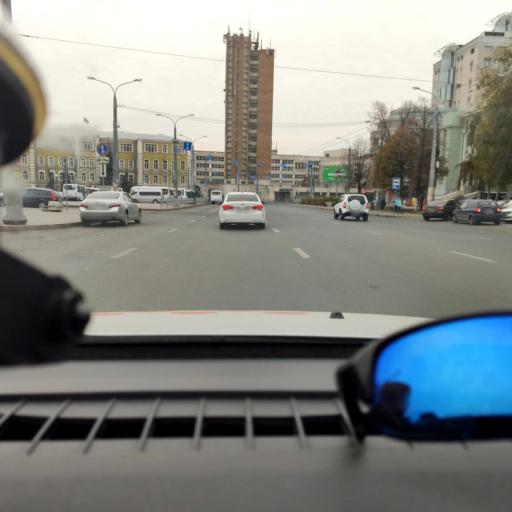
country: RU
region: Samara
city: Samara
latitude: 53.1880
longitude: 50.1190
